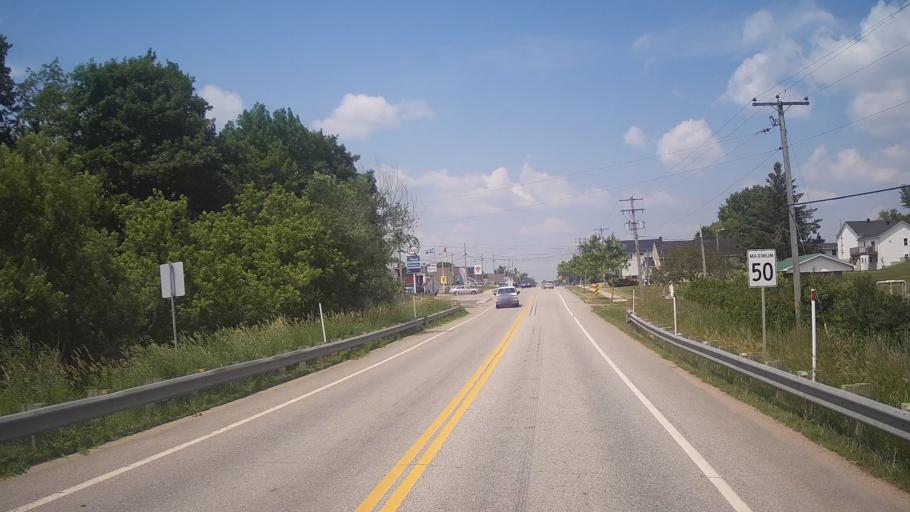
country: CA
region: Quebec
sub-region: Outaouais
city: Shawville
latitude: 45.5980
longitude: -76.4893
